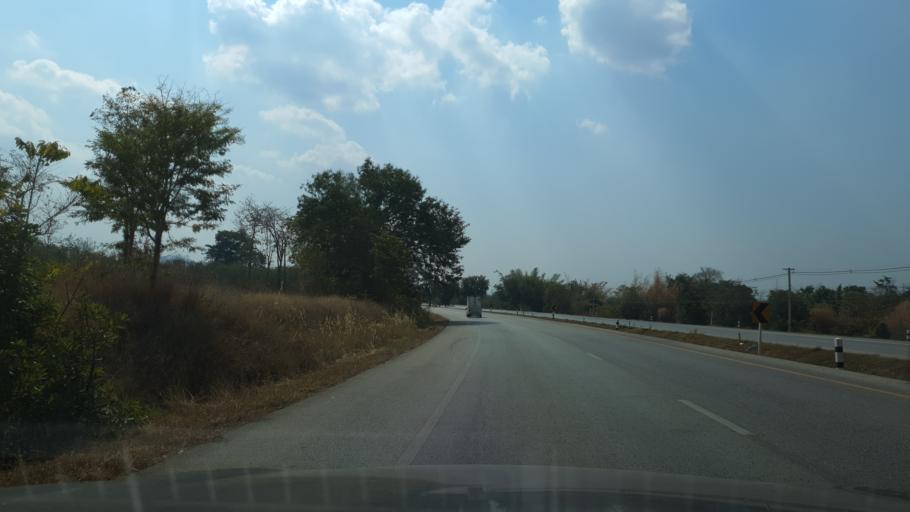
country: TH
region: Lampang
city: Mae Phrik
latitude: 17.4104
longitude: 99.1509
